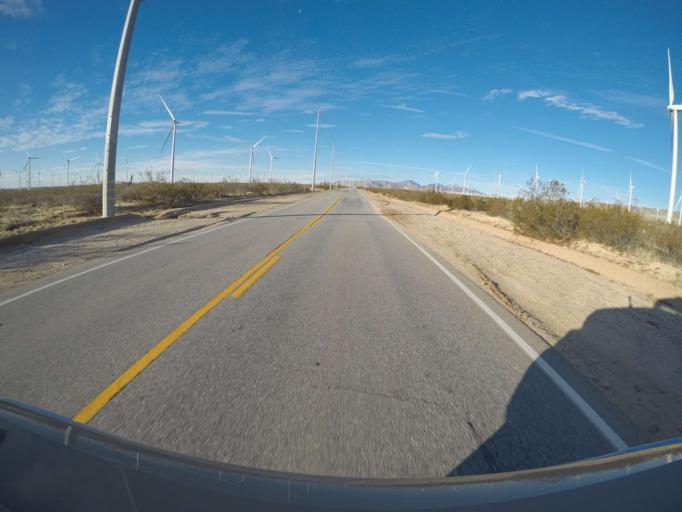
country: US
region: California
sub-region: Kern County
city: Mojave
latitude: 35.0444
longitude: -118.2244
